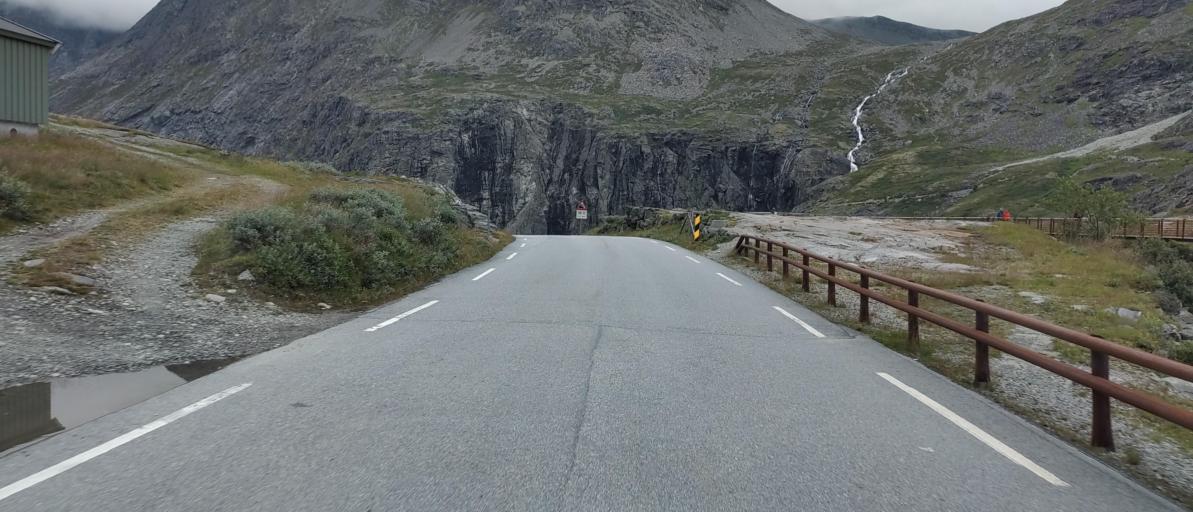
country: NO
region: More og Romsdal
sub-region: Rauma
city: Andalsnes
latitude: 62.4553
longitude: 7.6660
